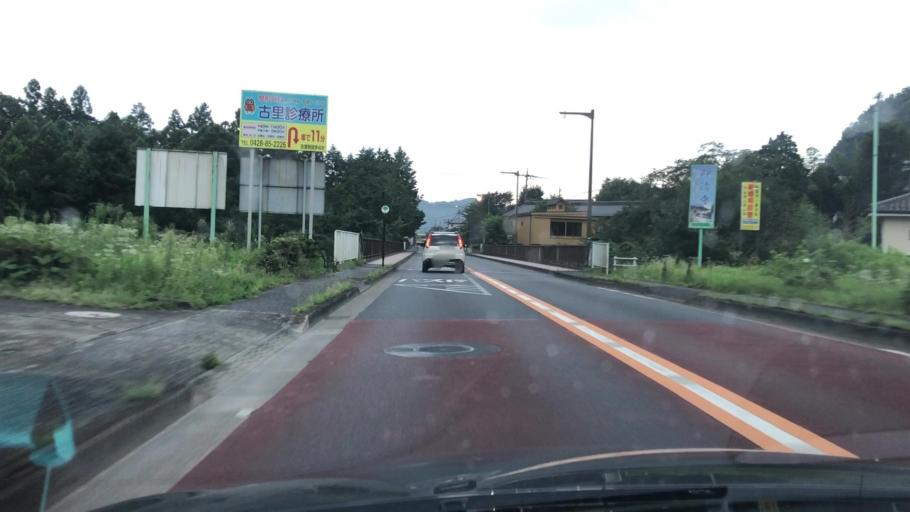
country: JP
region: Tokyo
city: Ome
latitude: 35.7943
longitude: 139.2148
